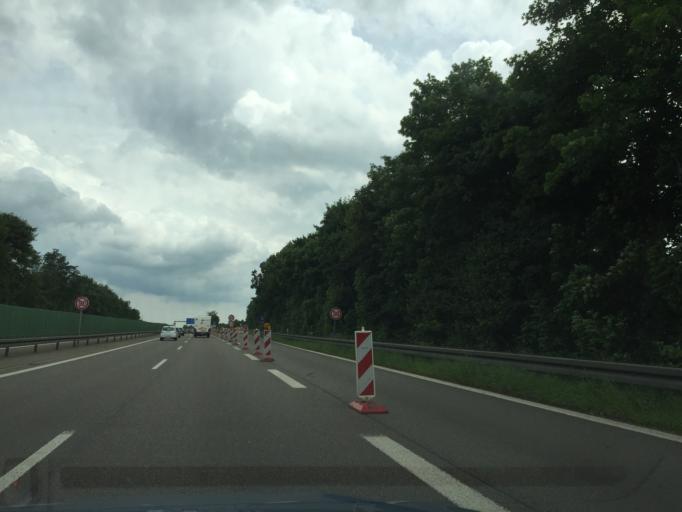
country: DE
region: Baden-Wuerttemberg
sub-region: Tuebingen Region
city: Ulm
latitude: 48.3667
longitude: 9.9875
